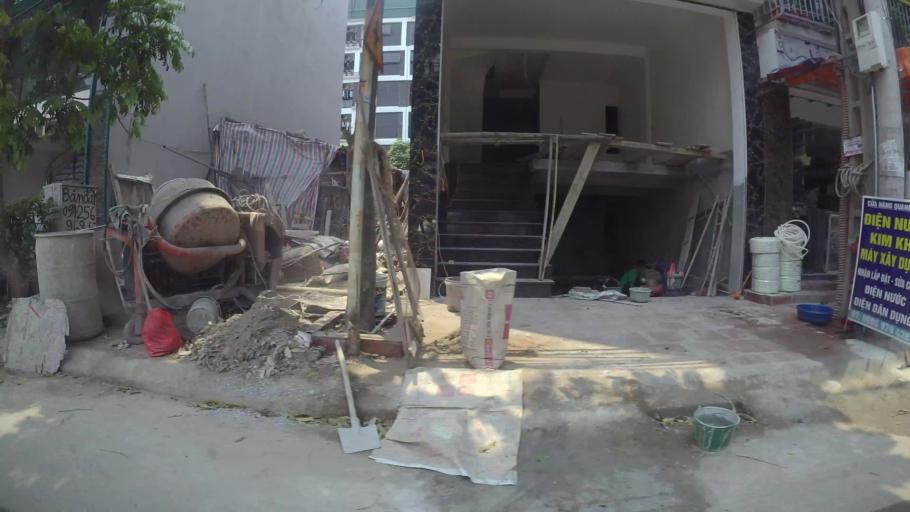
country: VN
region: Ha Noi
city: Ha Dong
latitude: 20.9952
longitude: 105.7724
